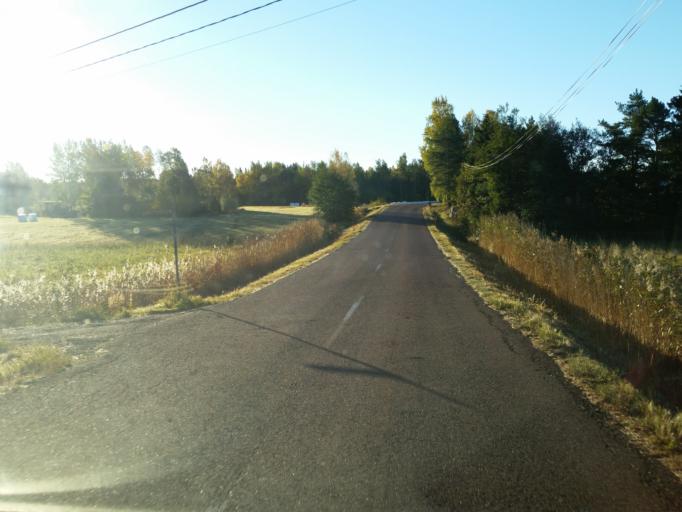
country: AX
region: Alands skaergard
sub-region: Vardoe
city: Vardoe
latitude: 60.2965
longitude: 20.3848
